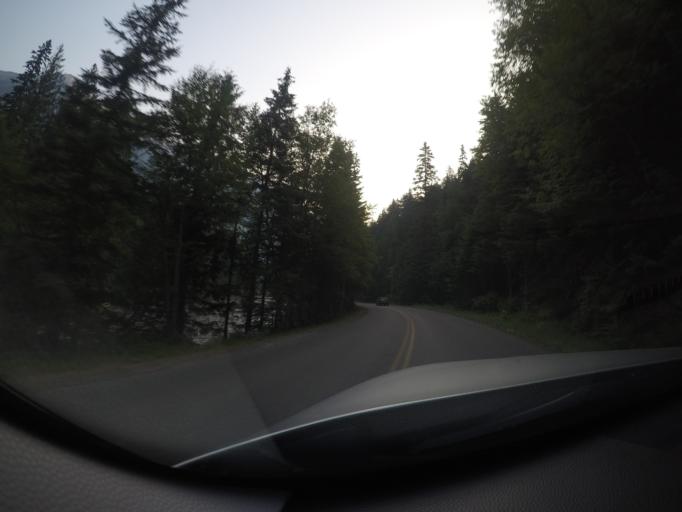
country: US
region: Montana
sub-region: Flathead County
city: Columbia Falls
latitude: 48.6998
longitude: -113.8122
